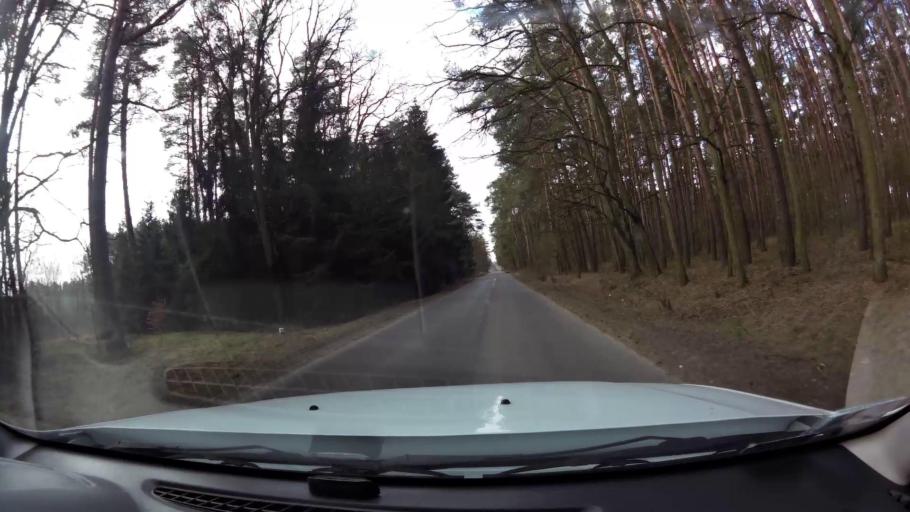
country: PL
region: West Pomeranian Voivodeship
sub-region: Powiat mysliborski
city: Debno
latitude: 52.8351
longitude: 14.6679
